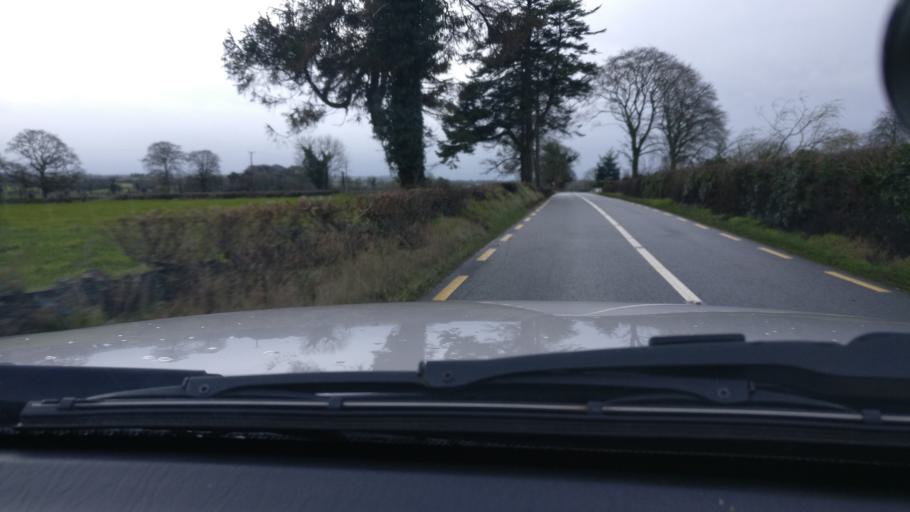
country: IE
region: Leinster
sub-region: An Longfort
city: Ballymahon
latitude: 53.5446
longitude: -7.7837
